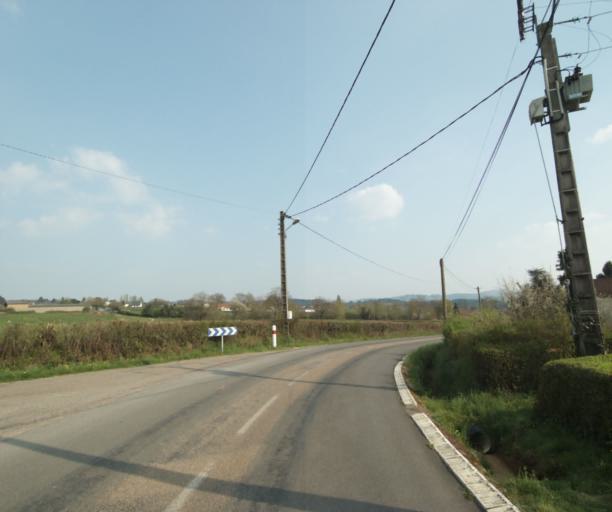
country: FR
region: Bourgogne
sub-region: Departement de Saone-et-Loire
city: Charolles
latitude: 46.4881
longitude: 4.4350
